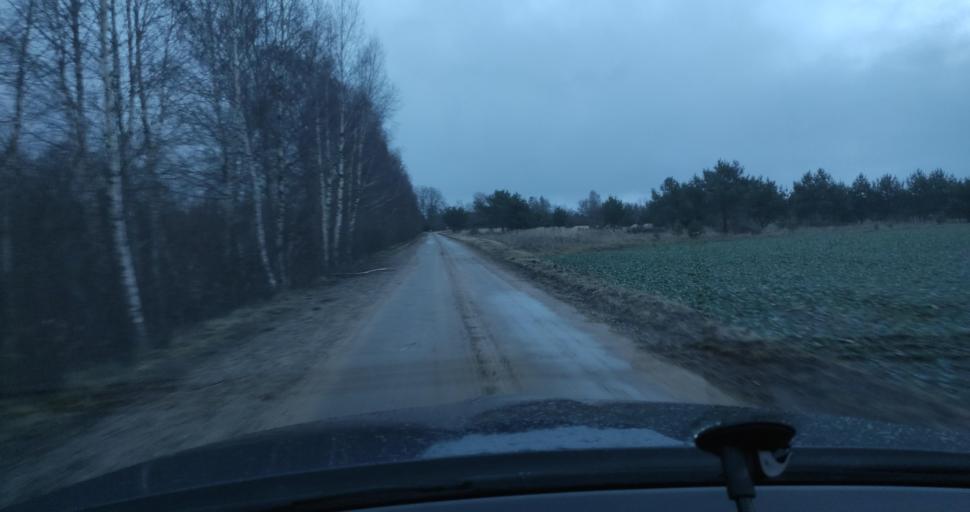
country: LV
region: Pavilostas
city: Pavilosta
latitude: 56.7368
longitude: 21.0699
